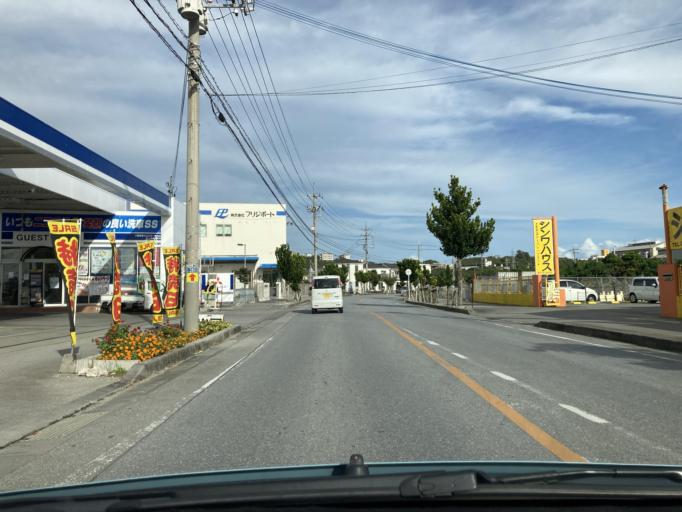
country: JP
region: Okinawa
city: Gushikawa
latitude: 26.3453
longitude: 127.8612
